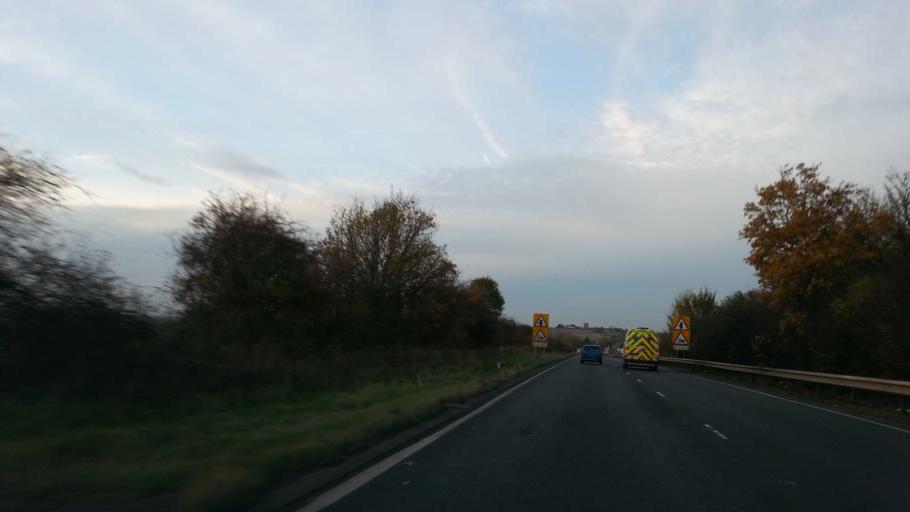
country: GB
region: England
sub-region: Central Bedfordshire
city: Stotfold
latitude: 52.0214
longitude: -0.2089
